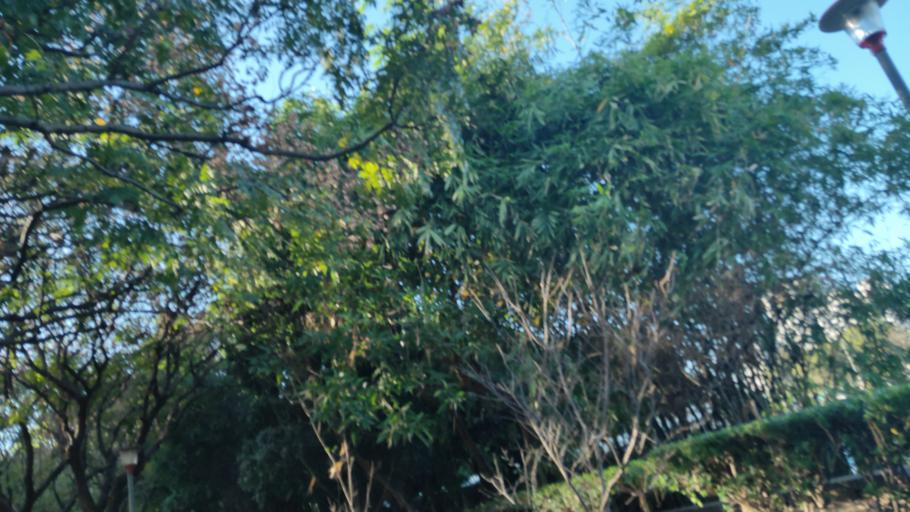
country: TW
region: Taiwan
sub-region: Taichung City
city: Taichung
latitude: 24.1409
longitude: 120.6110
